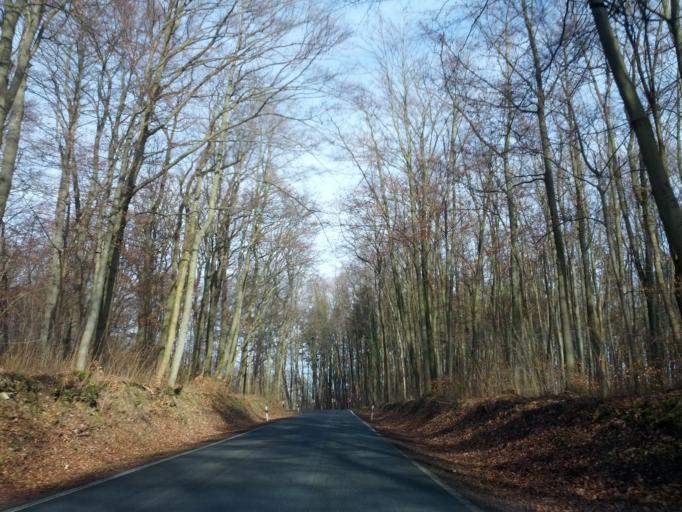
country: DE
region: Thuringia
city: Weberstedt
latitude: 51.0792
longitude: 10.5127
